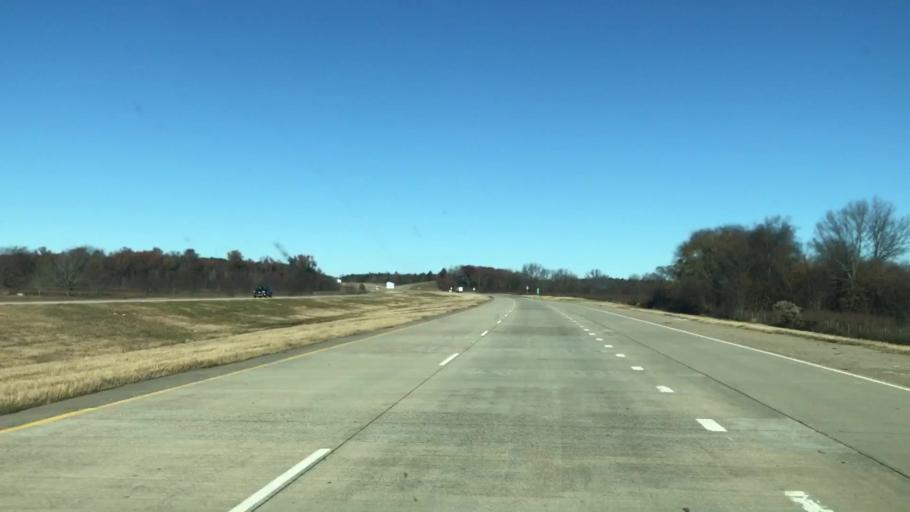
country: US
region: Louisiana
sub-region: Caddo Parish
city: Vivian
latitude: 32.9047
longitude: -93.8651
